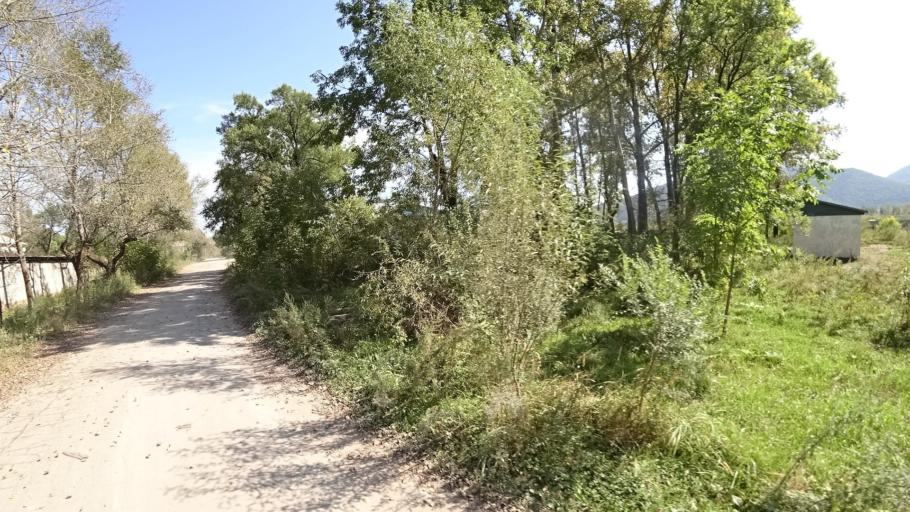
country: RU
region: Jewish Autonomous Oblast
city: Londoko
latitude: 49.0025
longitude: 131.8801
